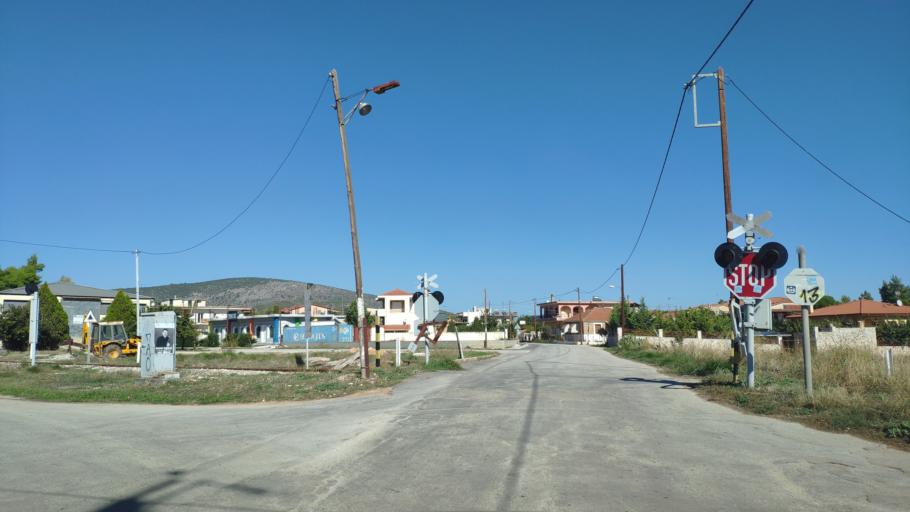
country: GR
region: Peloponnese
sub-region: Nomos Korinthias
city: Khiliomodhi
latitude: 37.8044
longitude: 22.8699
